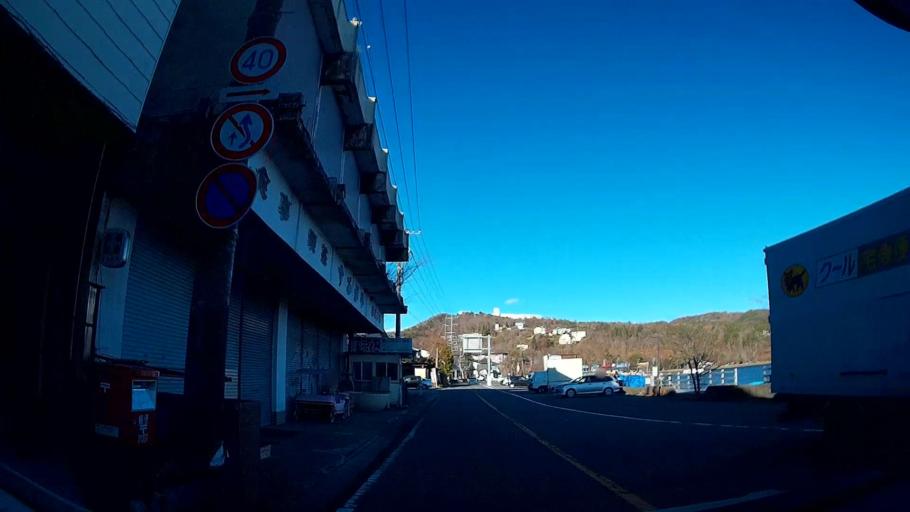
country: JP
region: Shizuoka
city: Gotemba
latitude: 35.4258
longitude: 138.8495
